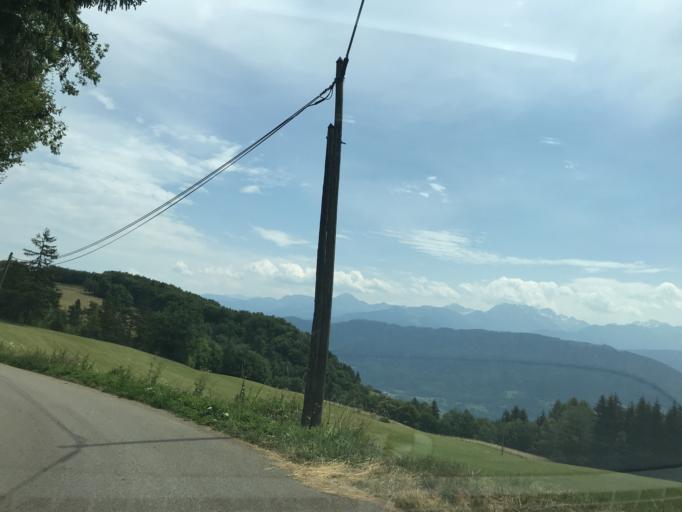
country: FR
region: Rhone-Alpes
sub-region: Departement de l'Isere
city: Barraux
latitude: 45.4114
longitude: 5.9487
